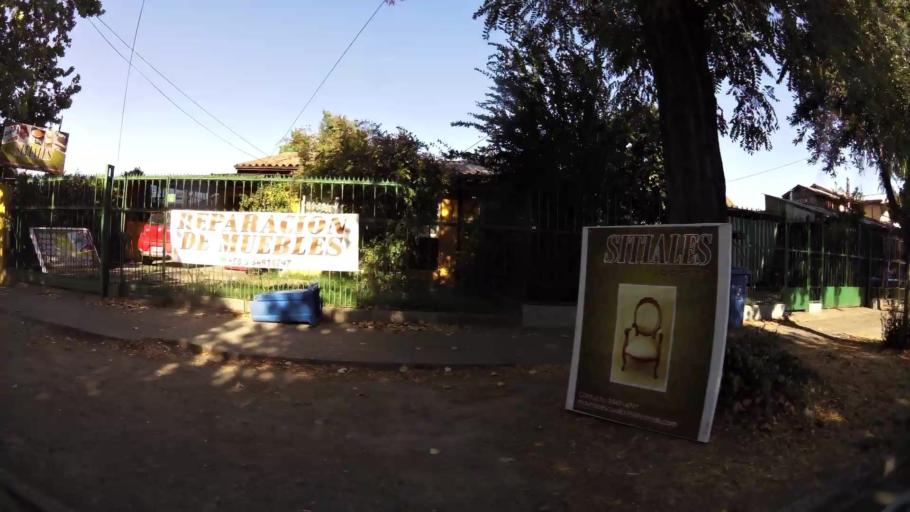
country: CL
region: Maule
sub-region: Provincia de Talca
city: Talca
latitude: -35.4374
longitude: -71.6663
